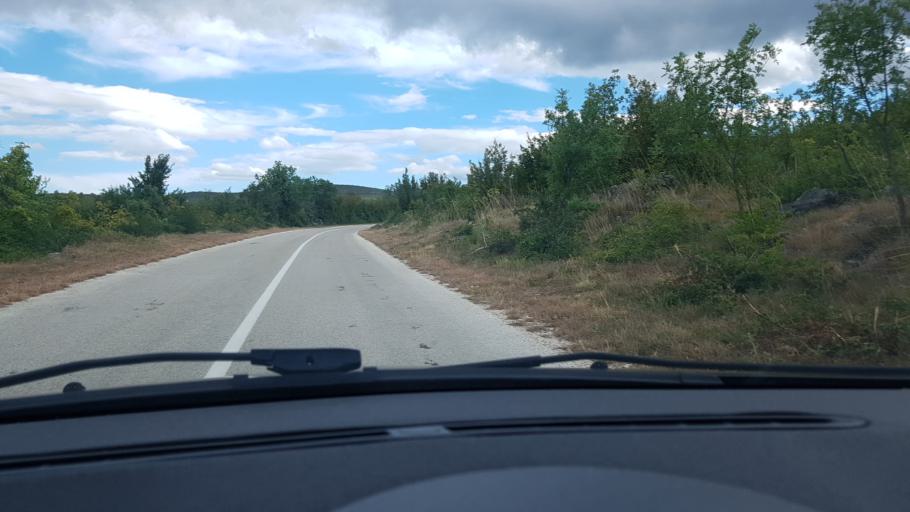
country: HR
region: Sibensko-Kniniska
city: Kistanje
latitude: 44.0976
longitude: 15.9365
